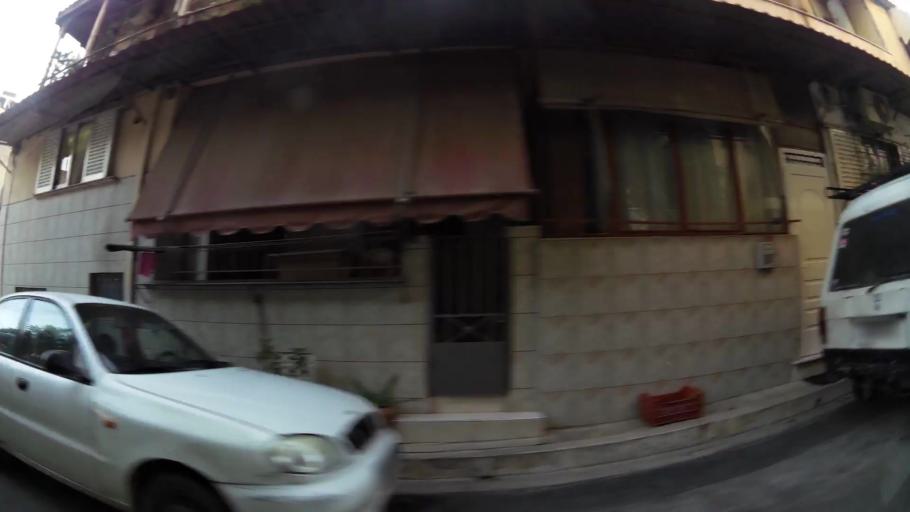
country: GR
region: Attica
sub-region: Nomos Piraios
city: Nikaia
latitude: 37.9708
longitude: 23.6432
